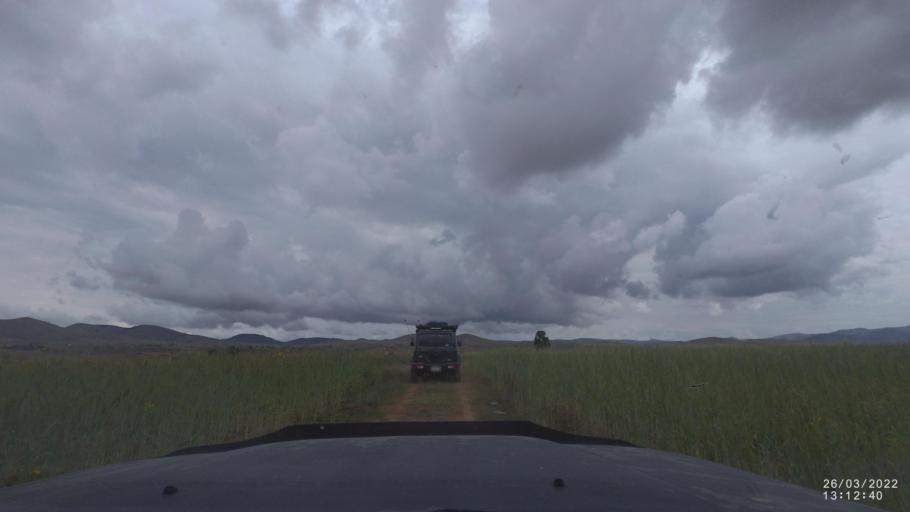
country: BO
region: Cochabamba
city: Cliza
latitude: -17.7370
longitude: -65.8617
